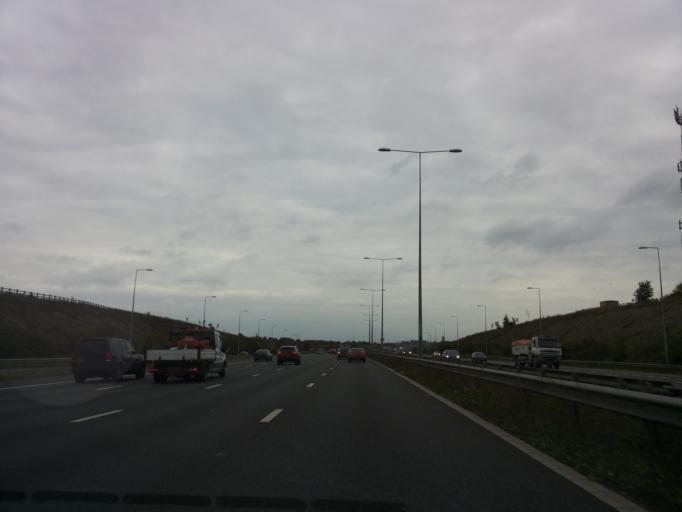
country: GB
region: England
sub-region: Kent
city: Gravesend
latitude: 51.4179
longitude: 0.3520
